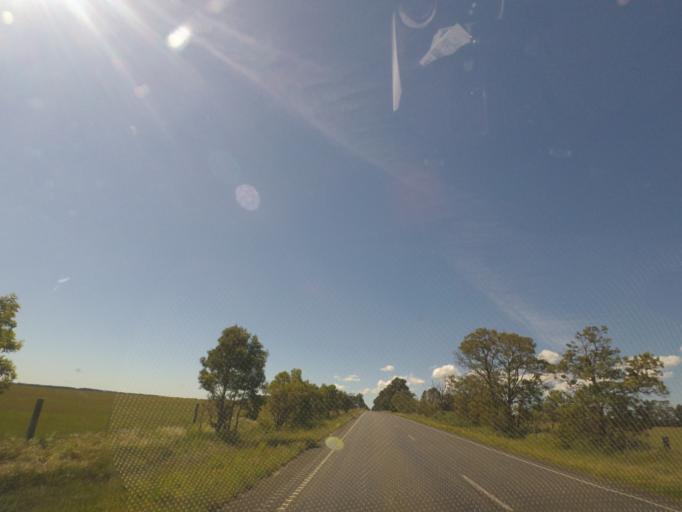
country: AU
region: Victoria
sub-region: Moorabool
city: Bacchus Marsh
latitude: -37.7733
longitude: 144.2169
